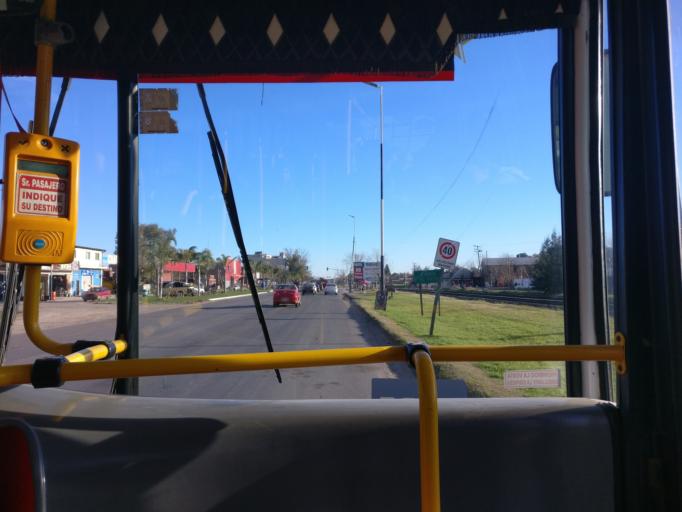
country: AR
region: Buenos Aires
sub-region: Partido de Ezeiza
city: Ezeiza
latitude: -34.8789
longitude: -58.5542
